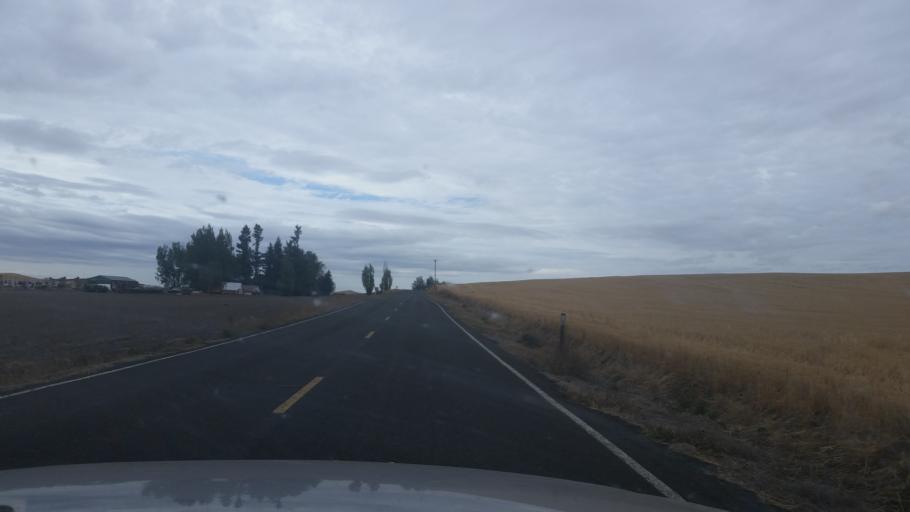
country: US
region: Washington
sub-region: Spokane County
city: Medical Lake
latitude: 47.5217
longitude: -117.8708
